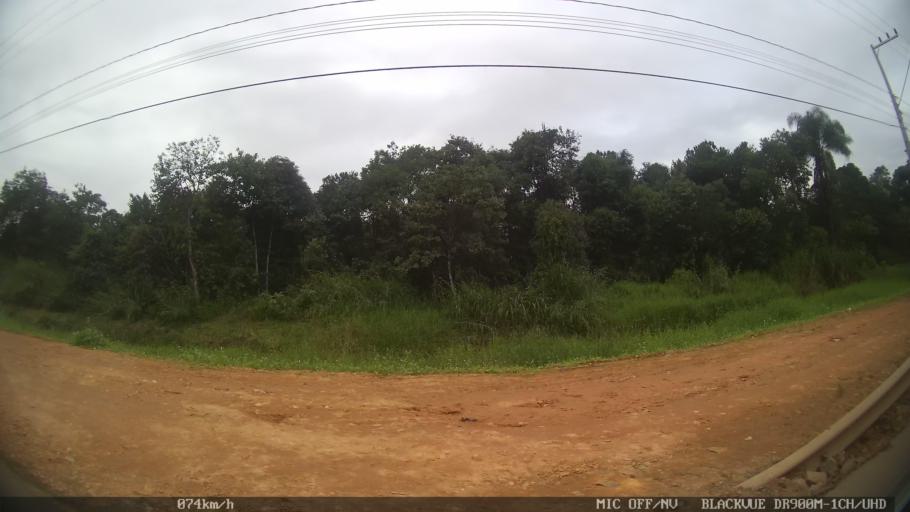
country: BR
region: Santa Catarina
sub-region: Joinville
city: Joinville
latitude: -26.2564
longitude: -48.8766
